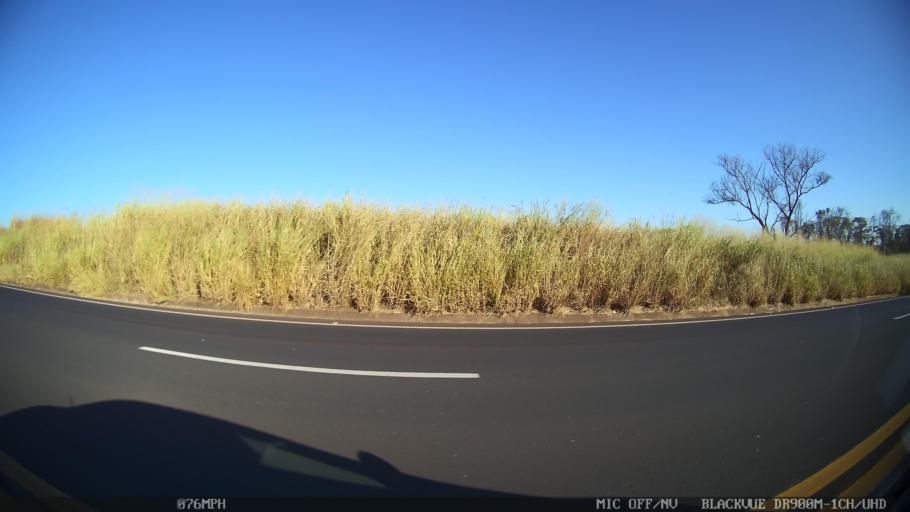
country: BR
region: Sao Paulo
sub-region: Guapiacu
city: Guapiacu
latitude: -20.7417
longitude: -49.0996
